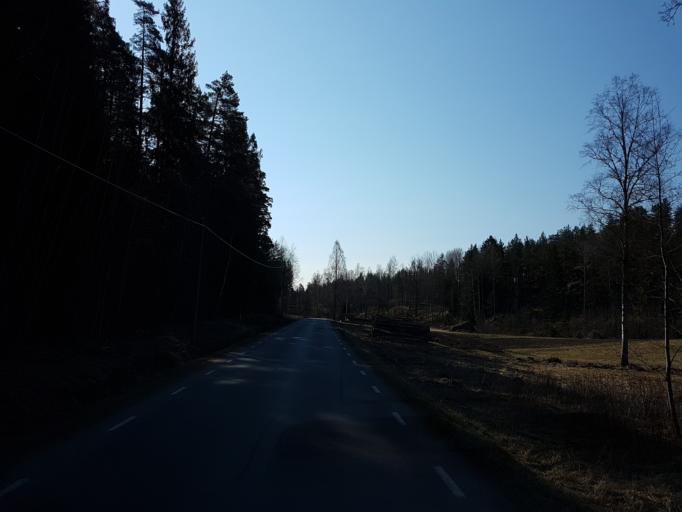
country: SE
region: Kalmar
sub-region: Vasterviks Kommun
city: Overum
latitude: 58.1553
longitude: 16.2252
